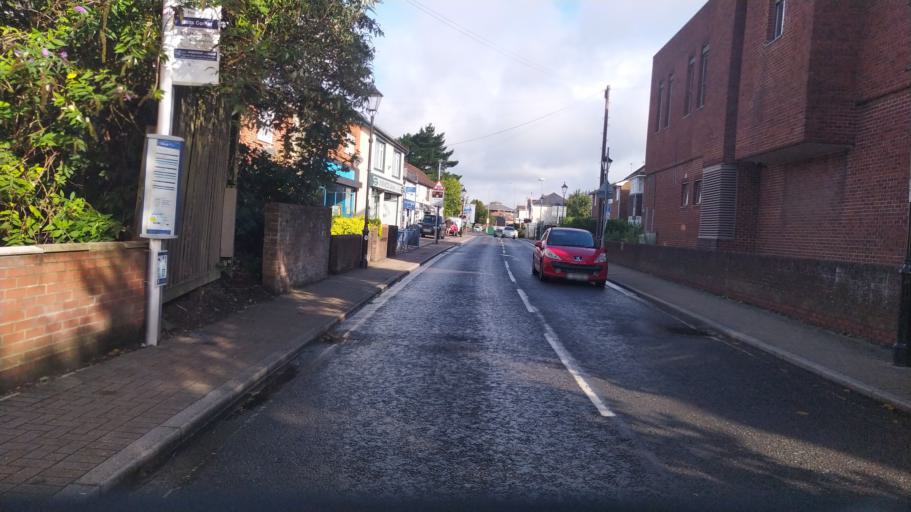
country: GB
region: England
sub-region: Hampshire
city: Totton
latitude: 50.9162
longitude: -1.4853
